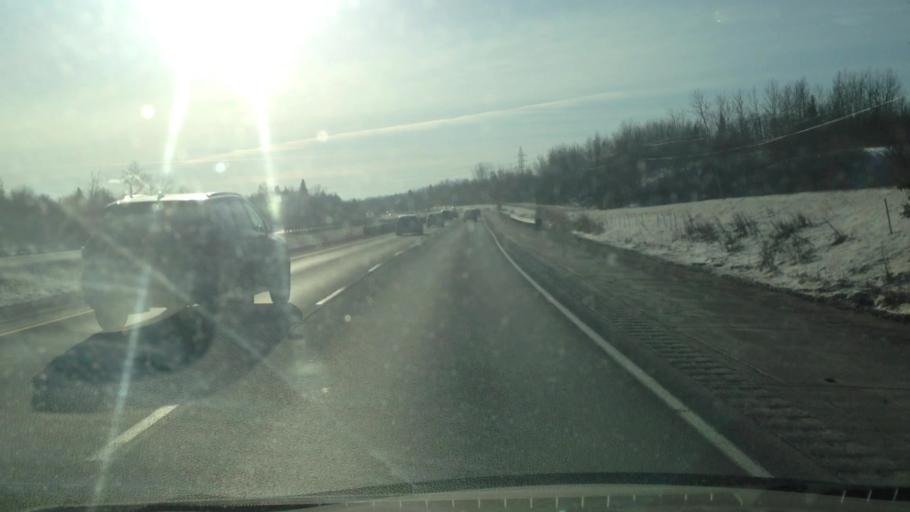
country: CA
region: Quebec
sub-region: Laurentides
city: Prevost
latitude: 45.8275
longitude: -74.0583
